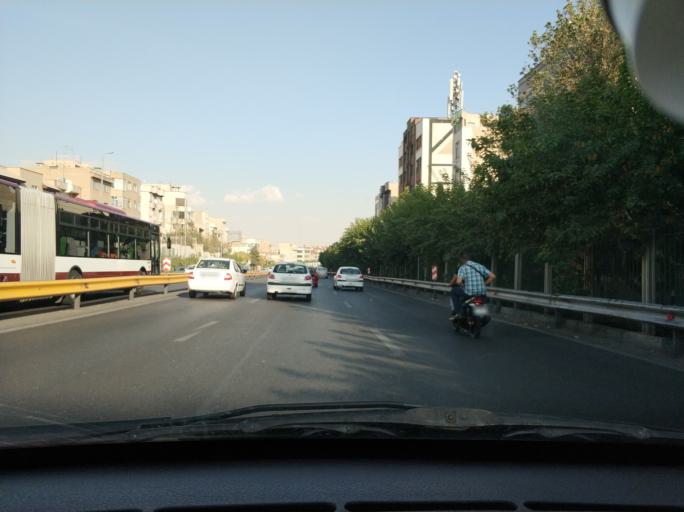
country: IR
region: Tehran
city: Tehran
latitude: 35.7426
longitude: 51.4411
